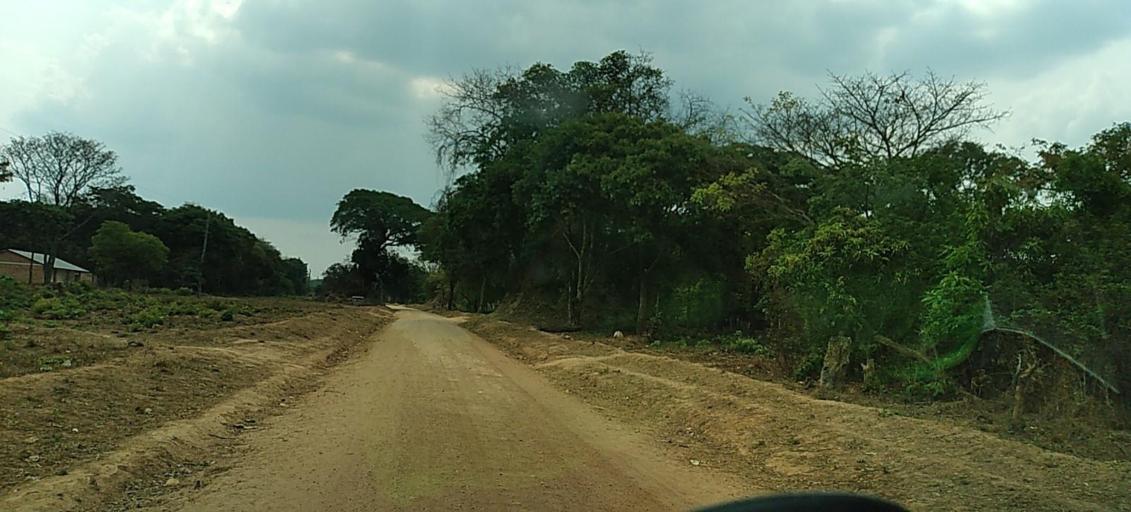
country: ZM
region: North-Western
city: Solwezi
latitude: -12.7851
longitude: 26.5128
